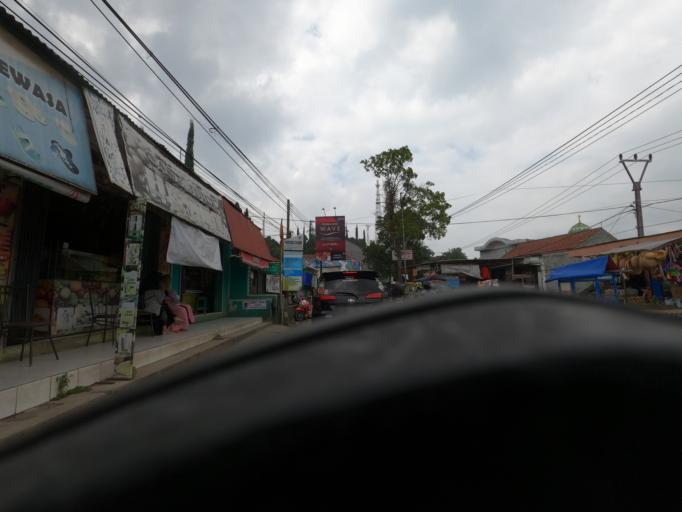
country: ID
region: West Java
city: Lembang
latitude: -6.8119
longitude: 107.5601
